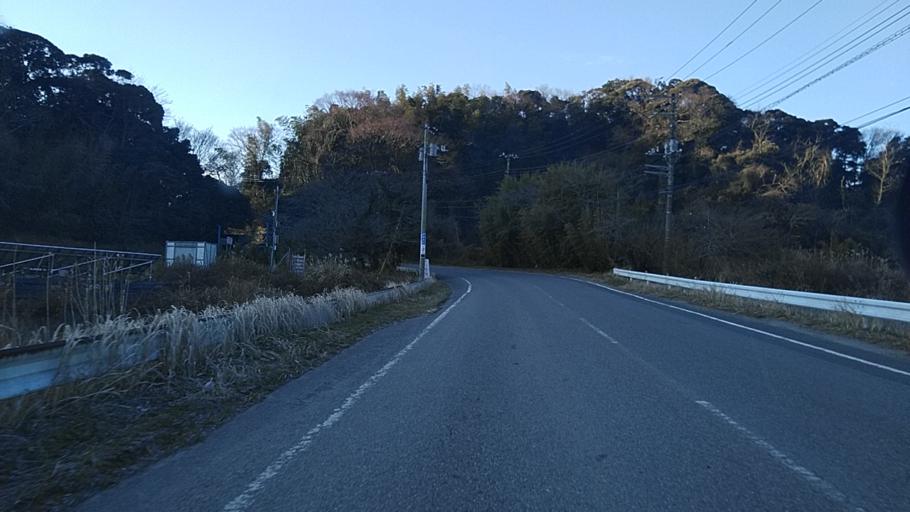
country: JP
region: Chiba
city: Kimitsu
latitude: 35.2719
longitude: 139.9203
